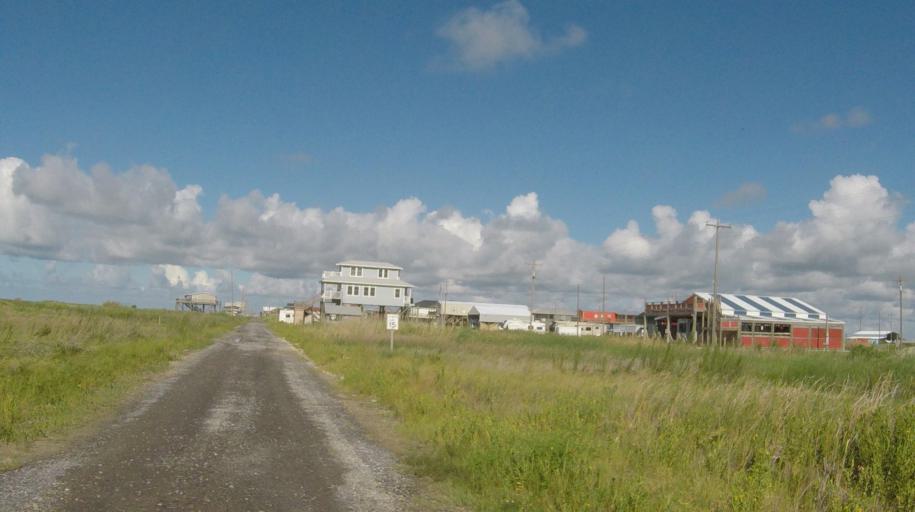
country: US
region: Louisiana
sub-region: Cameron Parish
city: Cameron
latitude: 29.7700
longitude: -93.4476
